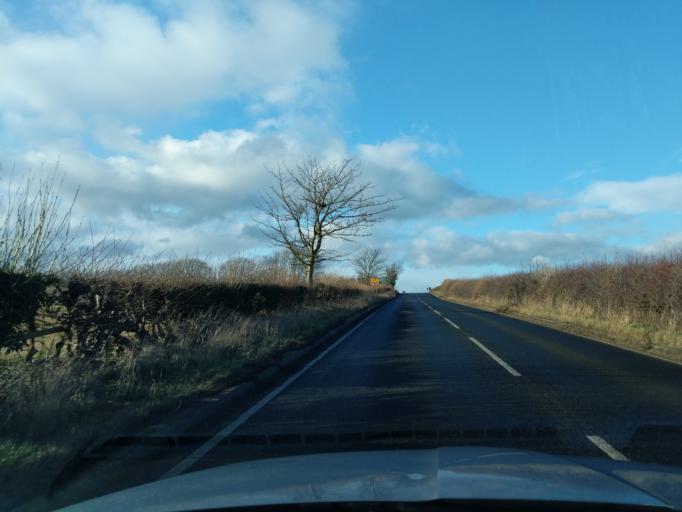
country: GB
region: England
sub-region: North Yorkshire
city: Catterick
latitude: 54.3166
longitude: -1.6750
